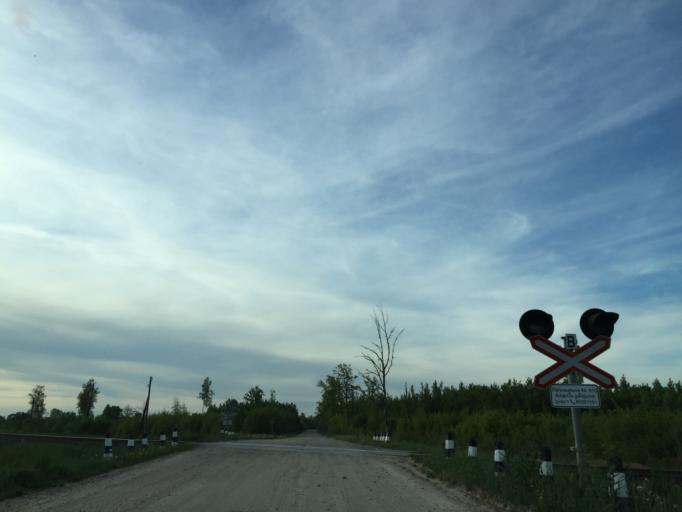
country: LV
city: Tireli
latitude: 56.6783
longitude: 23.5039
